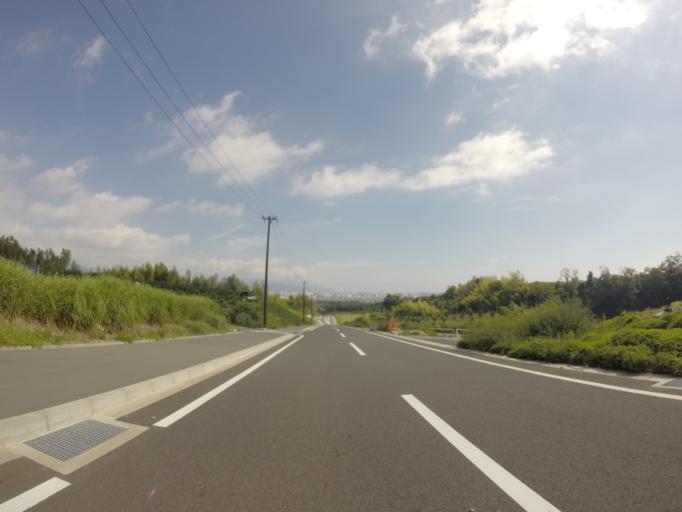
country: JP
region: Shizuoka
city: Shizuoka-shi
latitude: 34.9912
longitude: 138.4694
